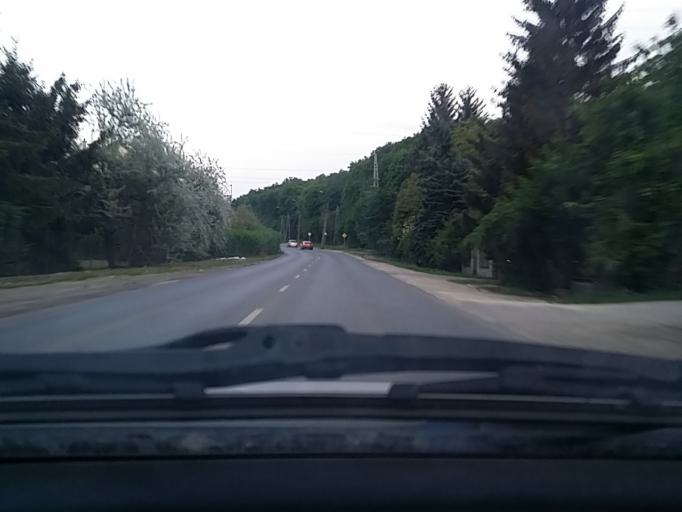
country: HU
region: Pest
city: Solymar
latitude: 47.5714
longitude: 18.9452
